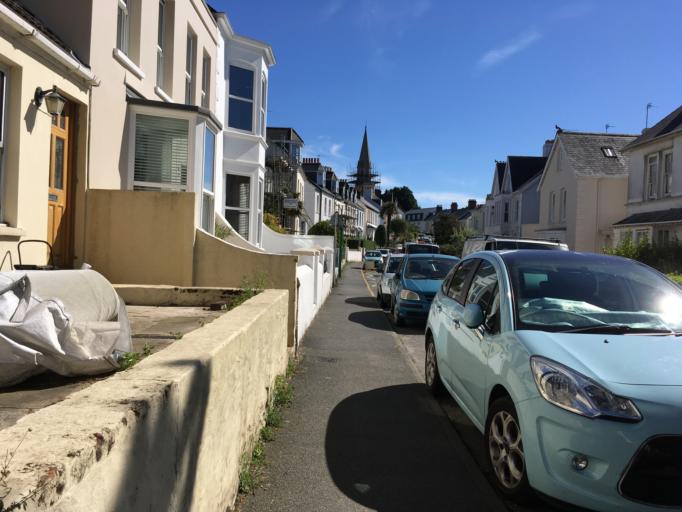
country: GG
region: St Peter Port
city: Saint Peter Port
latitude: 49.4582
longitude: -2.5464
